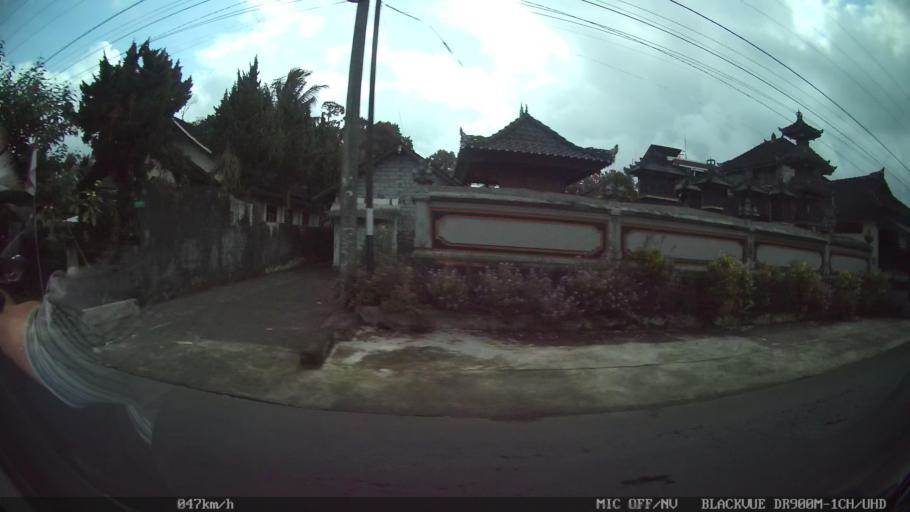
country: ID
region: Bali
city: Tunjuk Selatan
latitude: -8.4636
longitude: 115.1381
